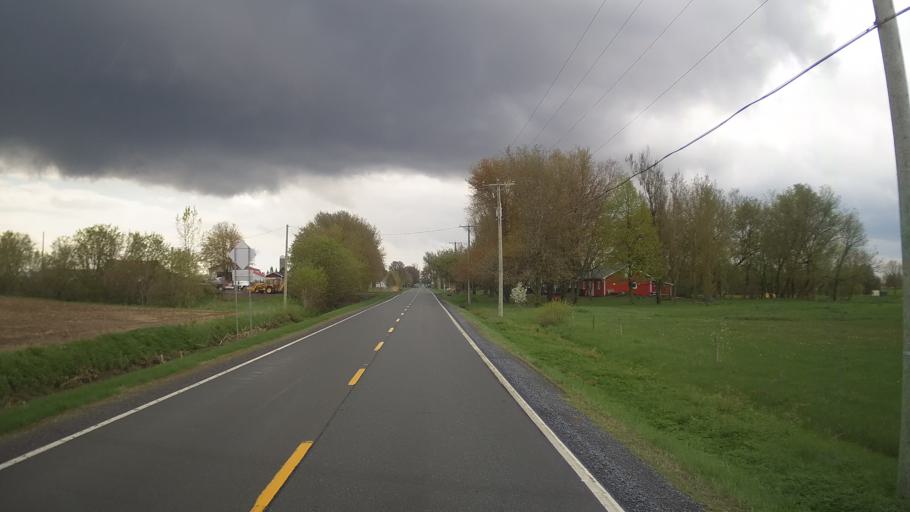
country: CA
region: Quebec
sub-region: Monteregie
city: Farnham
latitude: 45.3083
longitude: -73.1101
